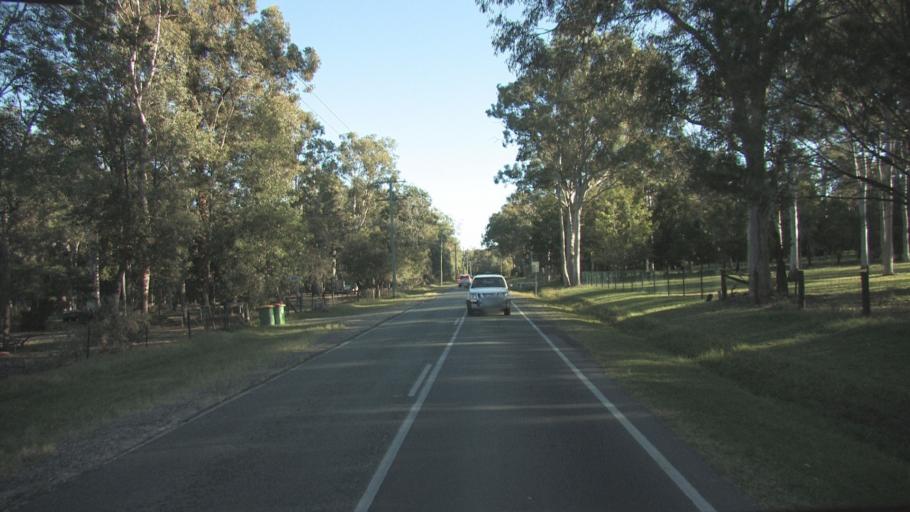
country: AU
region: Queensland
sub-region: Logan
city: Chambers Flat
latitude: -27.7528
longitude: 153.0524
